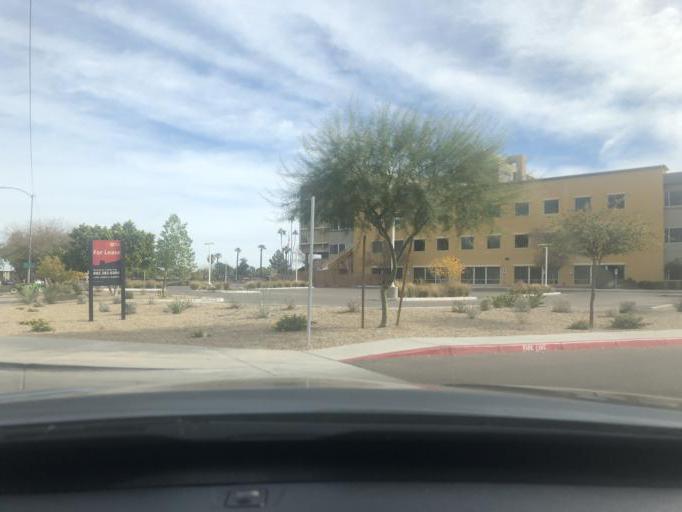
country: US
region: Arizona
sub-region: Maricopa County
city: Phoenix
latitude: 33.4555
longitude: -112.0442
